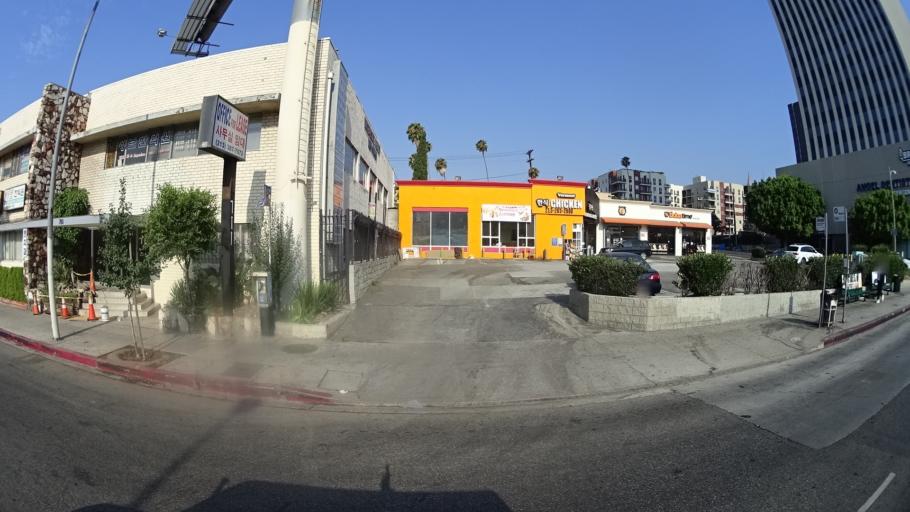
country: US
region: California
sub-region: Los Angeles County
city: Silver Lake
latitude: 34.0594
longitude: -118.2917
